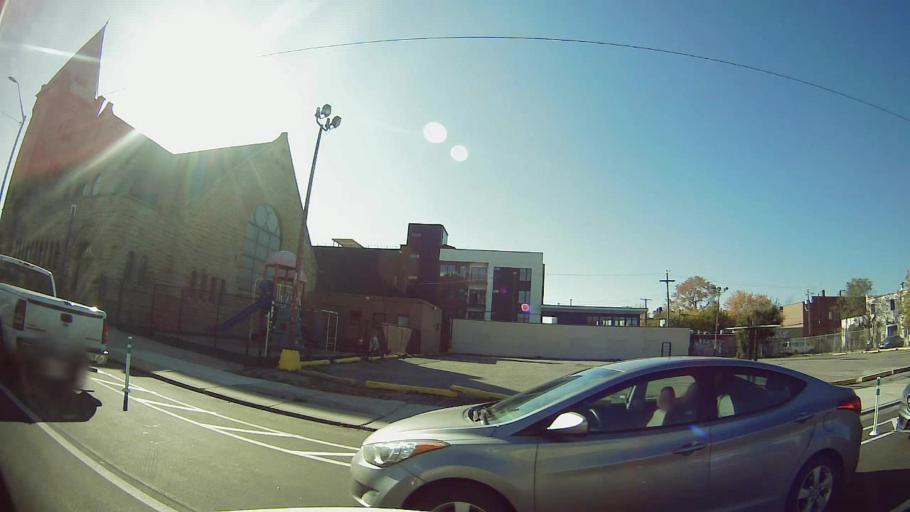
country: US
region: Michigan
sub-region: Wayne County
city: Detroit
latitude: 42.3486
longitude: -83.0624
